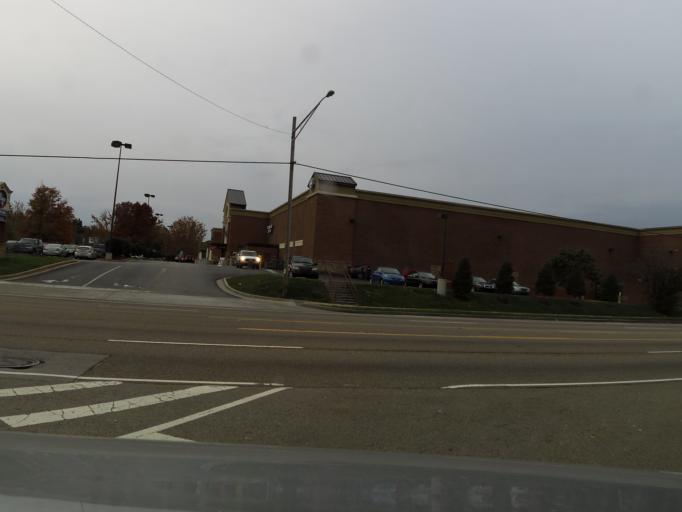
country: US
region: Tennessee
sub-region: Knox County
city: Knoxville
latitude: 36.0331
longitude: -83.9305
